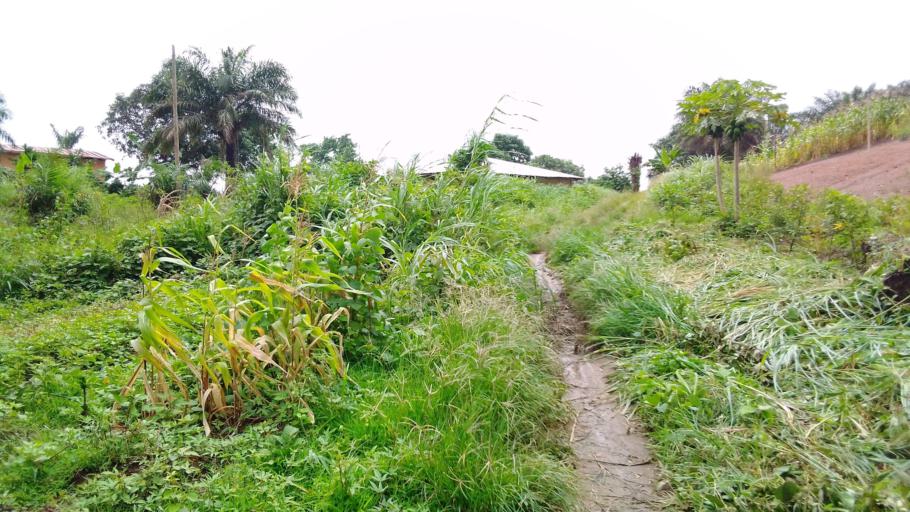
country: SL
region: Eastern Province
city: Kenema
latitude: 7.8731
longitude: -11.1704
